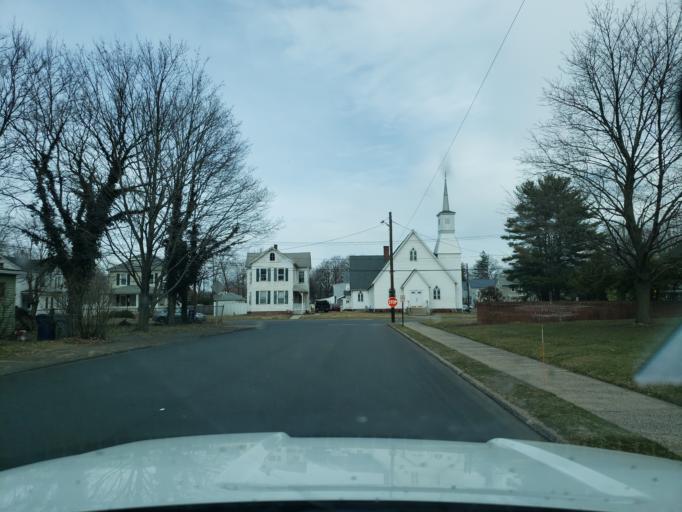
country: US
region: Connecticut
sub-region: Hartford County
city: Plainville
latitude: 41.6670
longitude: -72.8710
